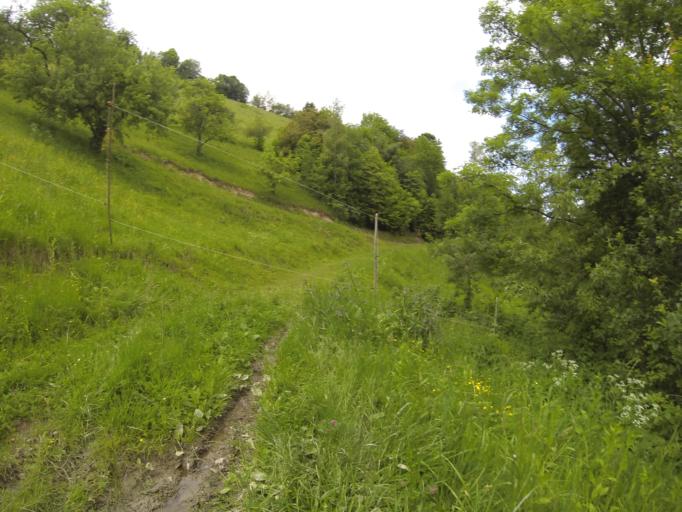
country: RO
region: Brasov
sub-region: Comuna Poiana Marului
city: Poiana Marului
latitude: 45.6473
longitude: 25.2882
